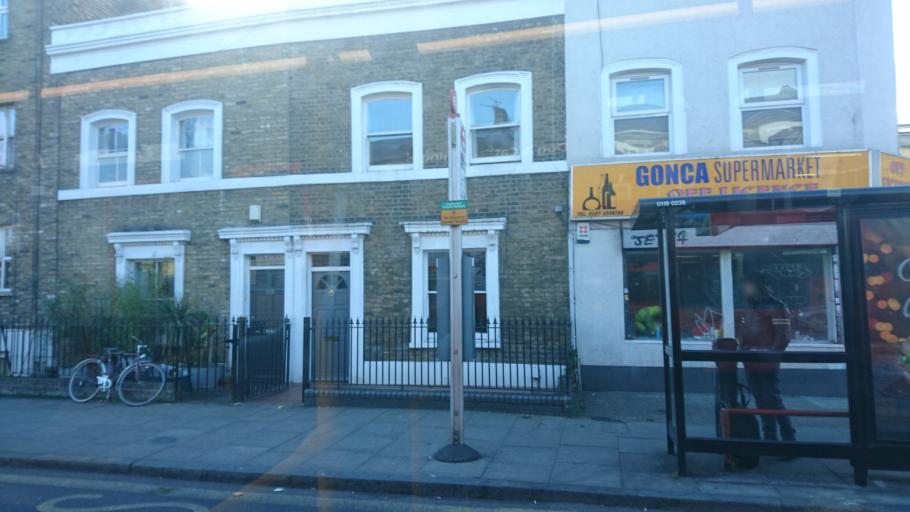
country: GB
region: England
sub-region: Greater London
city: Harringay
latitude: 51.5618
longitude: -0.0999
